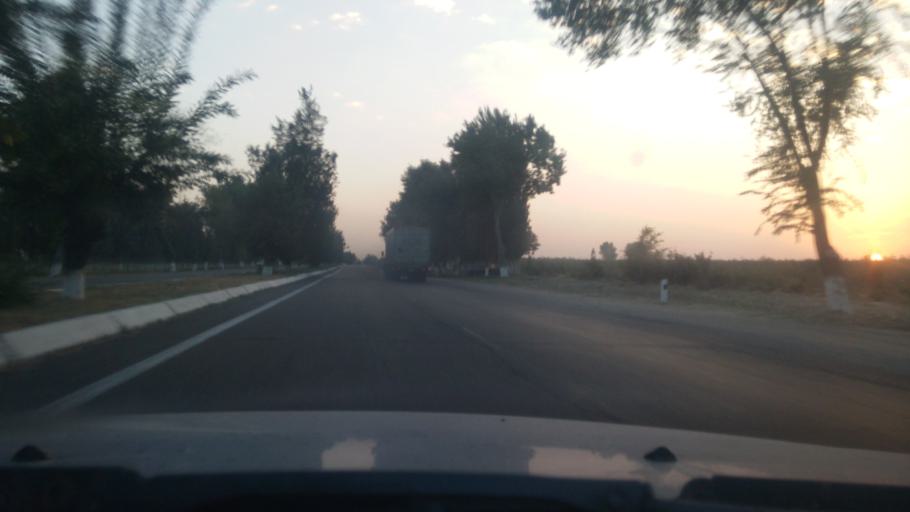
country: UZ
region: Toshkent
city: Zafar
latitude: 41.0009
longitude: 68.8223
